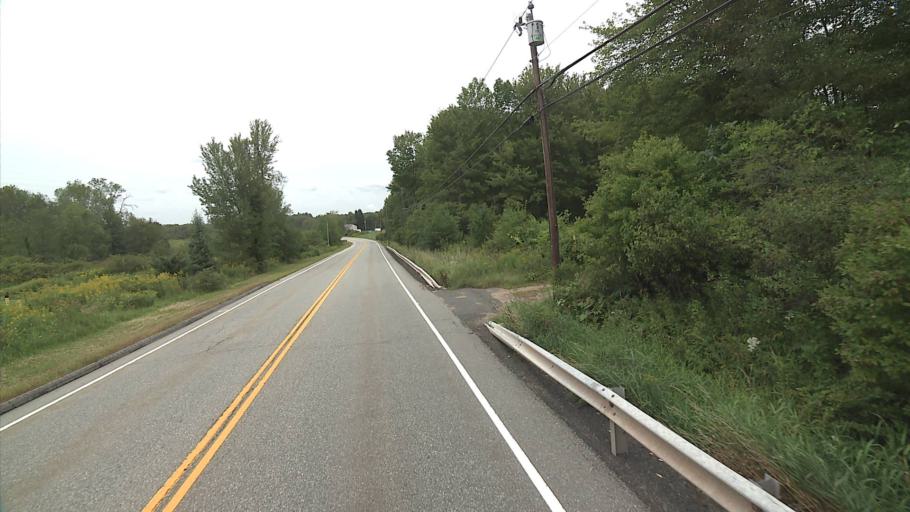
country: US
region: Connecticut
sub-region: Hartford County
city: Terramuggus
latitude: 41.7094
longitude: -72.4328
